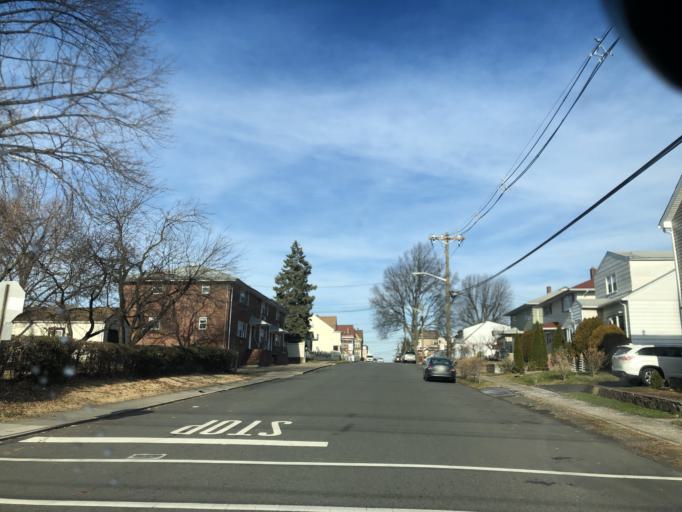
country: US
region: New Jersey
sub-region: Bergen County
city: Fair Lawn
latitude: 40.9297
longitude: -74.1464
